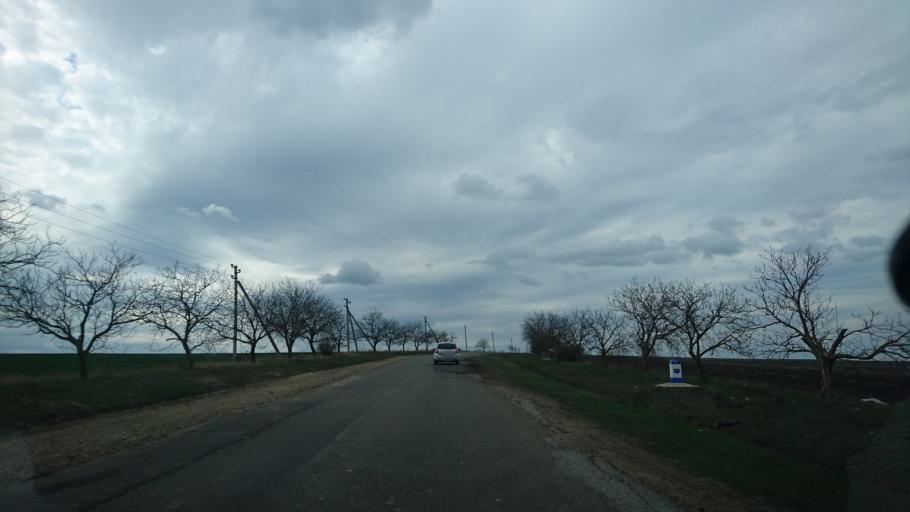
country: MD
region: Cantemir
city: Visniovca
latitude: 46.3190
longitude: 28.5478
